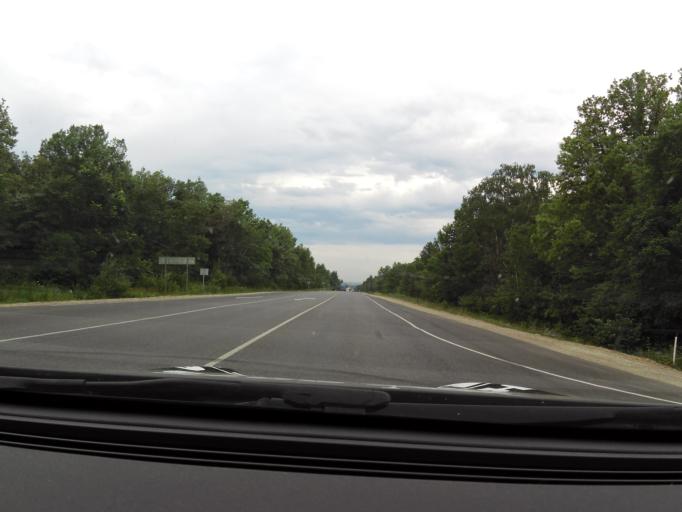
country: RU
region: Bashkortostan
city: Ulu-Telyak
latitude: 54.8384
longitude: 57.0316
